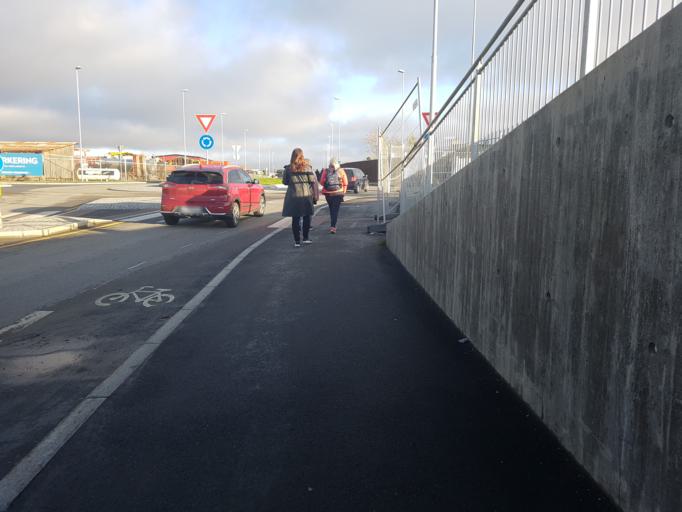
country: NO
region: Akershus
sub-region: Ullensaker
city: Jessheim
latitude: 60.1443
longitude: 11.1794
